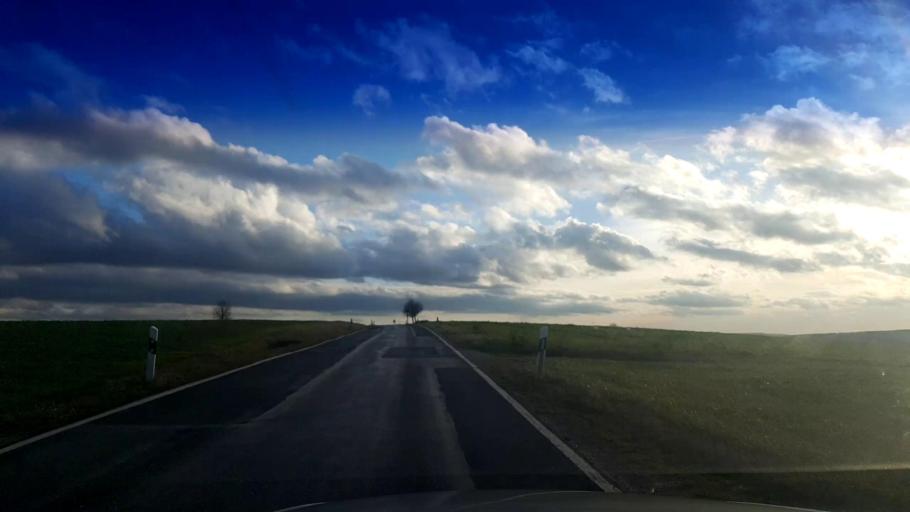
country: DE
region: Bavaria
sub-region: Upper Franconia
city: Buttenheim
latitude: 49.8195
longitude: 11.0257
